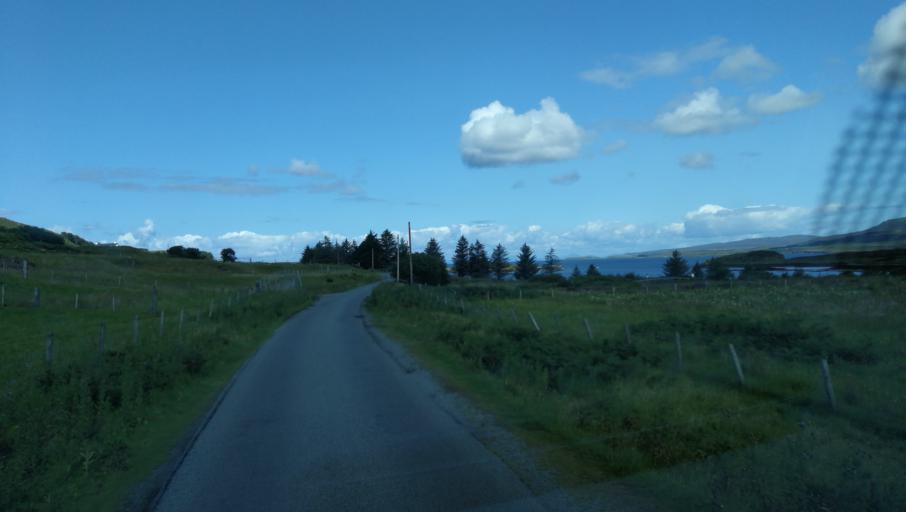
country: GB
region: Scotland
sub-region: Highland
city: Isle of Skye
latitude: 57.4397
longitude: -6.6378
